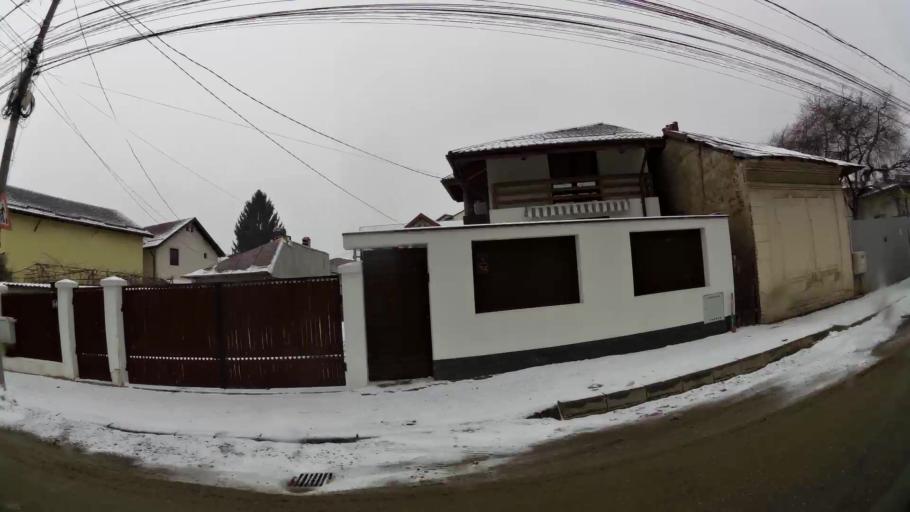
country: RO
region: Dambovita
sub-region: Municipiul Targoviste
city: Targoviste
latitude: 44.9238
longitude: 25.4698
